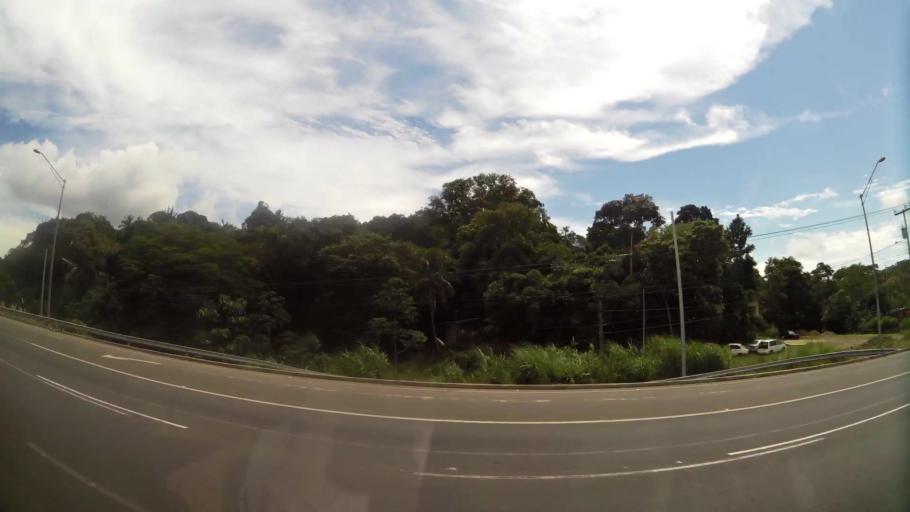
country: PA
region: Panama
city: San Vicente de Bique
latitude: 8.9325
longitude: -79.6839
